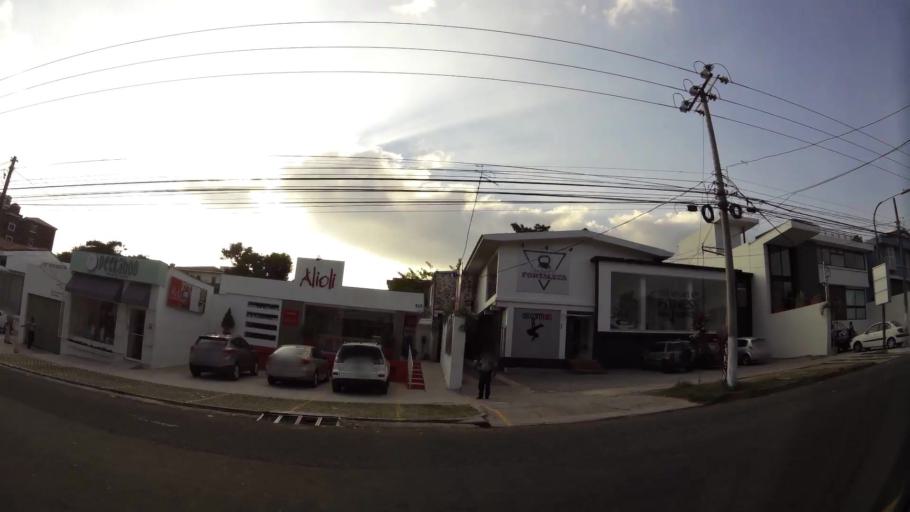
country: SV
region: La Libertad
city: Antiguo Cuscatlan
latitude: 13.6910
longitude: -89.2441
